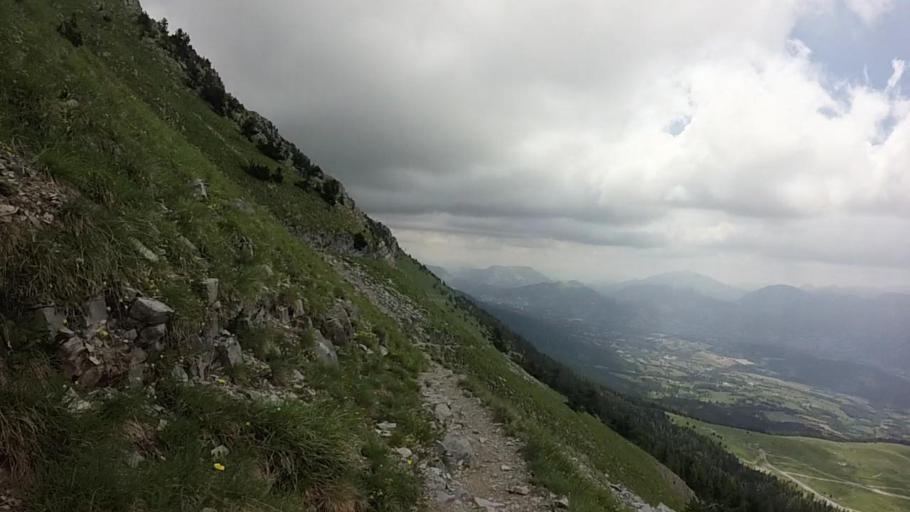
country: FR
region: Provence-Alpes-Cote d'Azur
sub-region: Departement des Alpes-de-Haute-Provence
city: Seyne-les-Alpes
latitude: 44.4038
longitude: 6.3831
